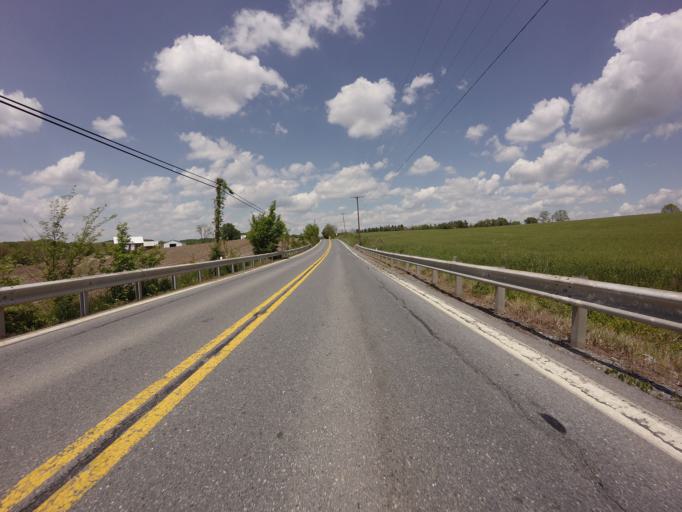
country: US
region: Maryland
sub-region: Frederick County
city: Green Valley
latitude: 39.3036
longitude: -77.3026
